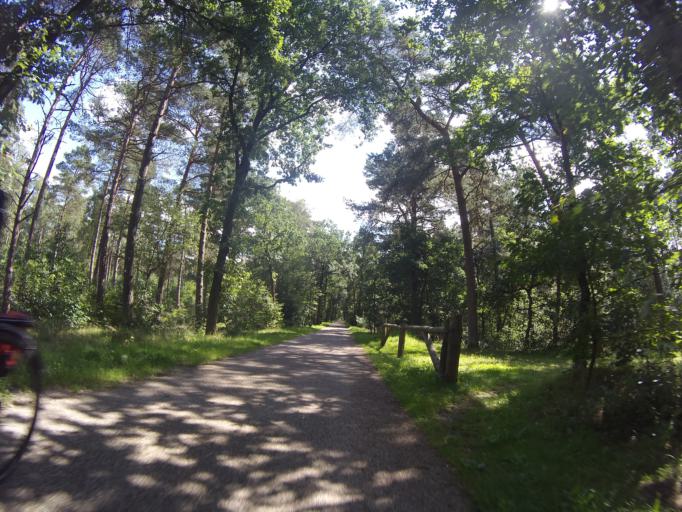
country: NL
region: Utrecht
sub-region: Gemeente Soest
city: Soest
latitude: 52.1495
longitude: 5.2735
